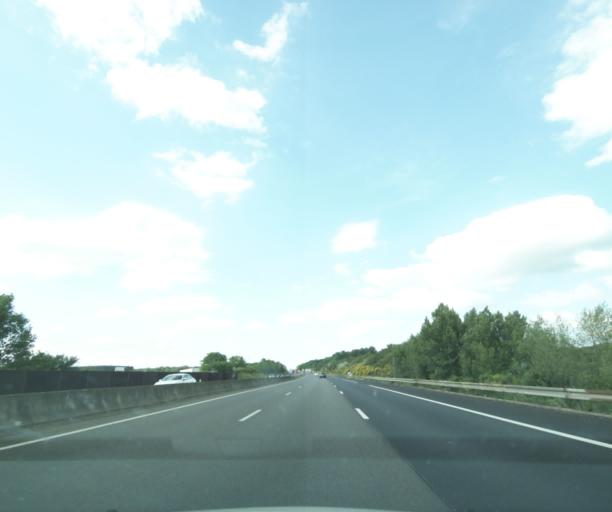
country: FR
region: Centre
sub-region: Departement du Loiret
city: Saint-Jean-de-la-Ruelle
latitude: 47.9287
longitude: 1.8495
